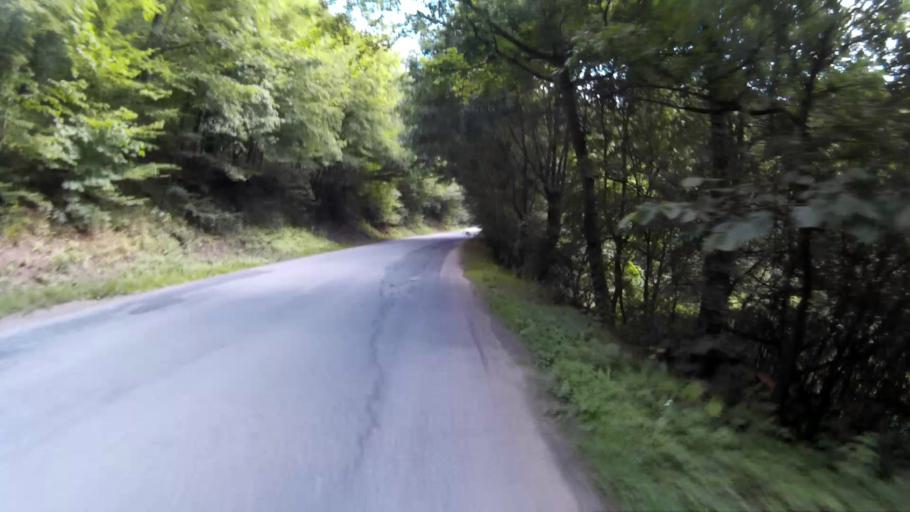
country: CZ
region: South Moravian
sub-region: Okres Brno-Venkov
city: Rosice
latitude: 49.1645
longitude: 16.4362
